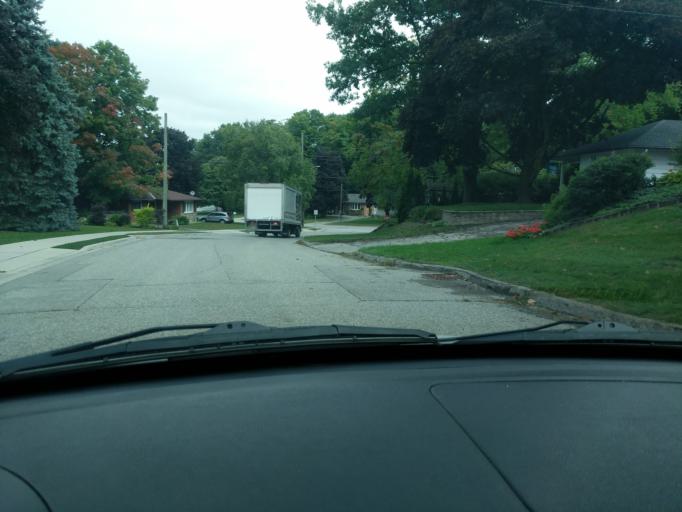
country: CA
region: Ontario
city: Cambridge
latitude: 43.4206
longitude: -80.3143
